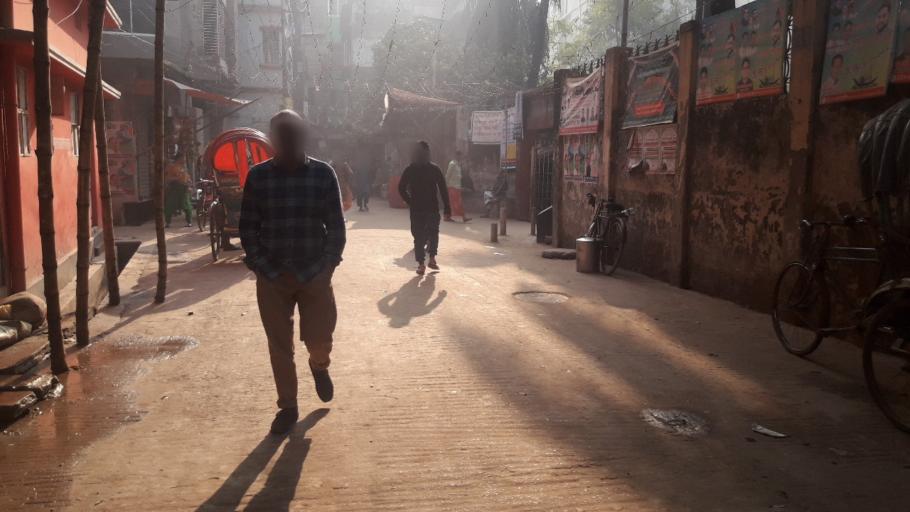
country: BD
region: Dhaka
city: Azimpur
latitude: 23.7220
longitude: 90.3766
